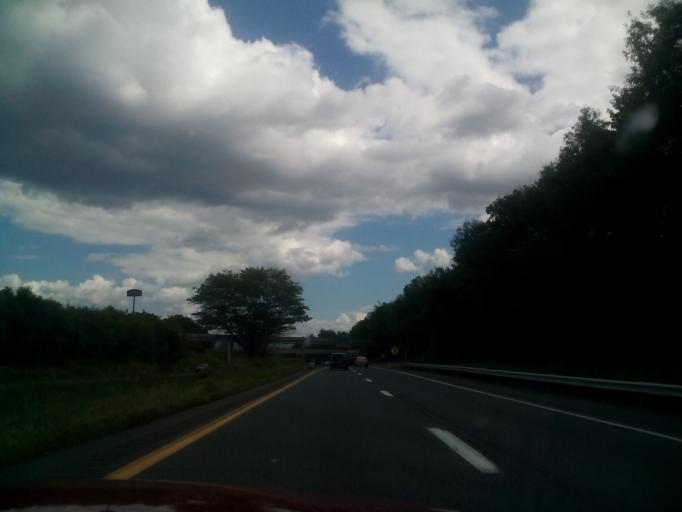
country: US
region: Pennsylvania
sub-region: Monroe County
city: Tannersville
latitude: 40.9989
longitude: -75.2722
